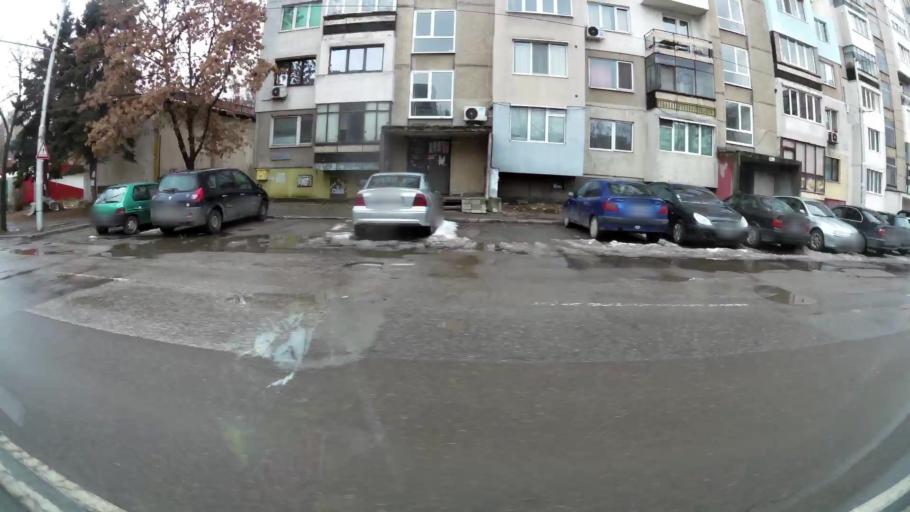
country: BG
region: Sofiya
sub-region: Obshtina Bozhurishte
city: Bozhurishte
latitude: 42.7277
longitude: 23.2510
